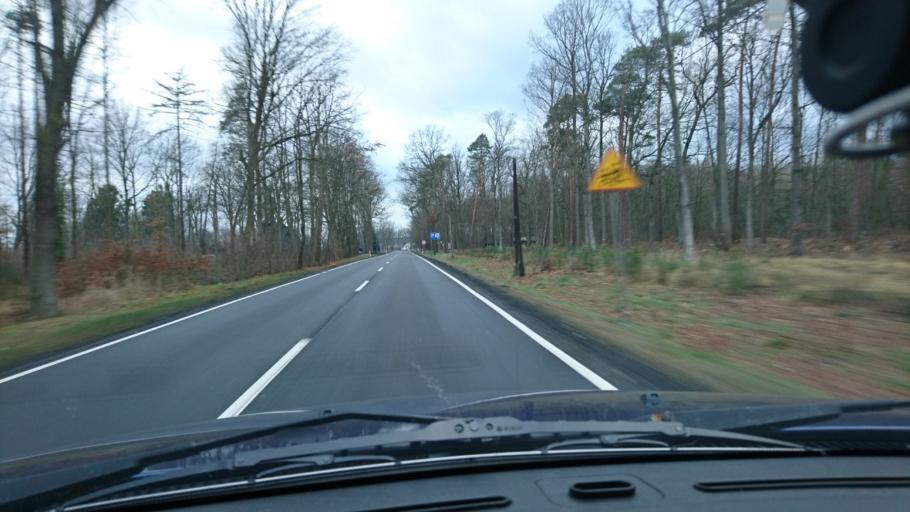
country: PL
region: Opole Voivodeship
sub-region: Powiat oleski
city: Olesno
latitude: 50.9089
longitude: 18.3610
